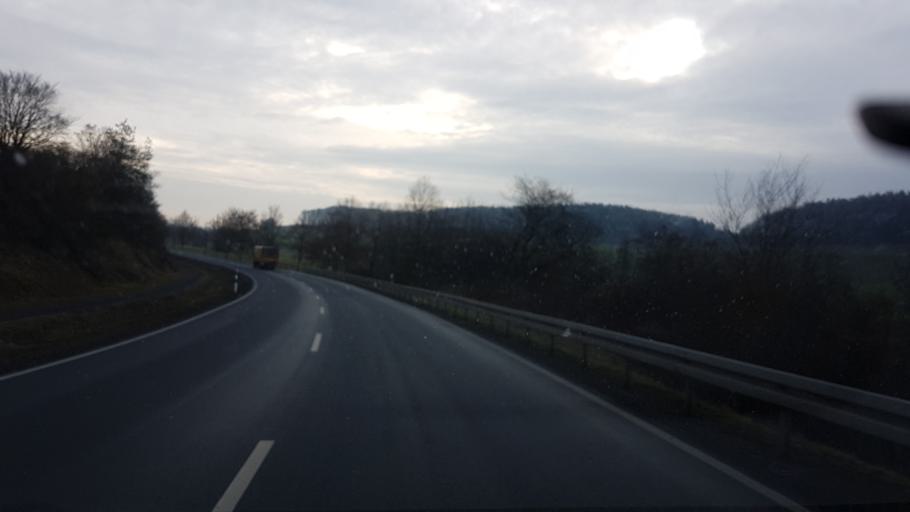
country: DE
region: Bavaria
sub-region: Regierungsbezirk Unterfranken
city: Pfarrweisach
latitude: 50.1660
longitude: 10.7206
